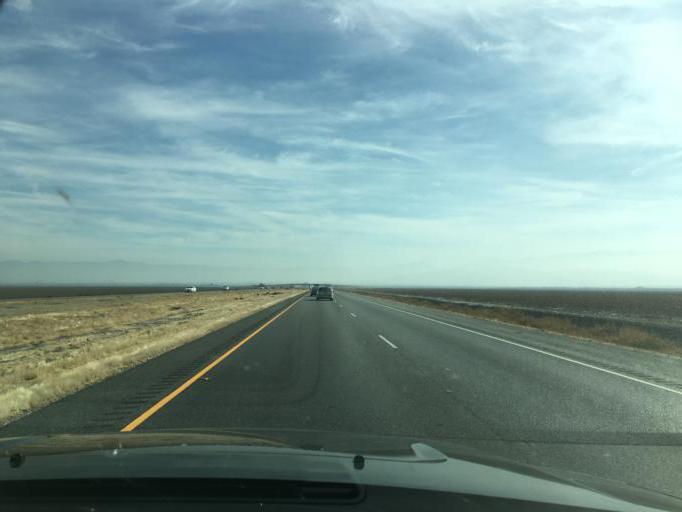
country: US
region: California
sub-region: Kern County
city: Greenfield
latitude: 35.1366
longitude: -119.0833
